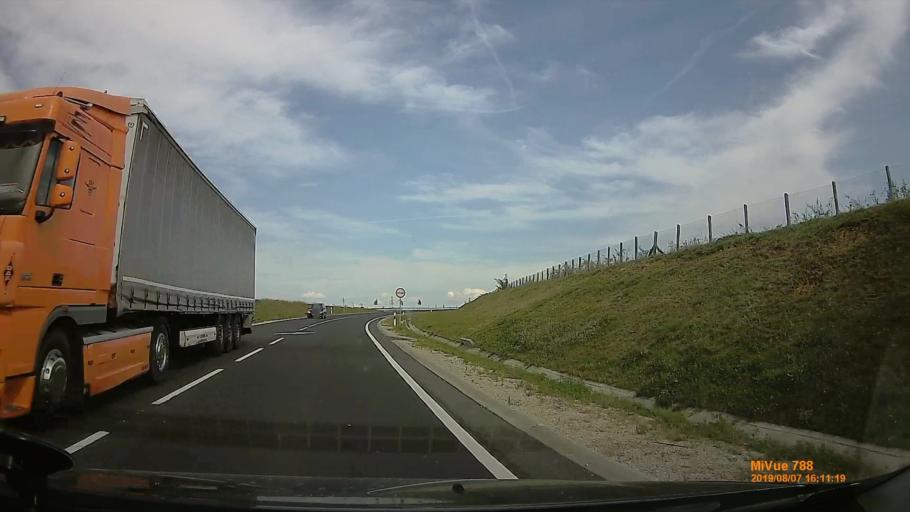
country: HU
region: Zala
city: Zalalovo
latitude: 46.8715
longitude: 16.6199
